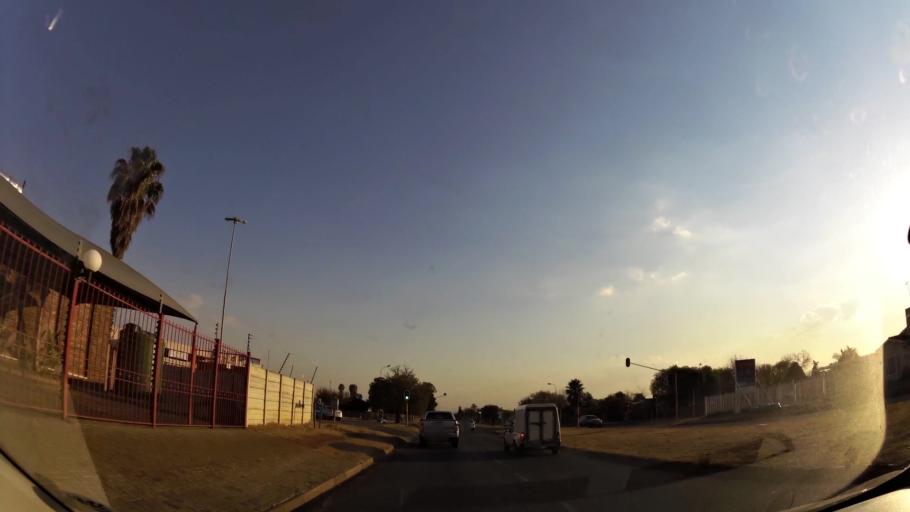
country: ZA
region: Gauteng
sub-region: Ekurhuleni Metropolitan Municipality
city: Boksburg
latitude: -26.2627
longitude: 28.2328
